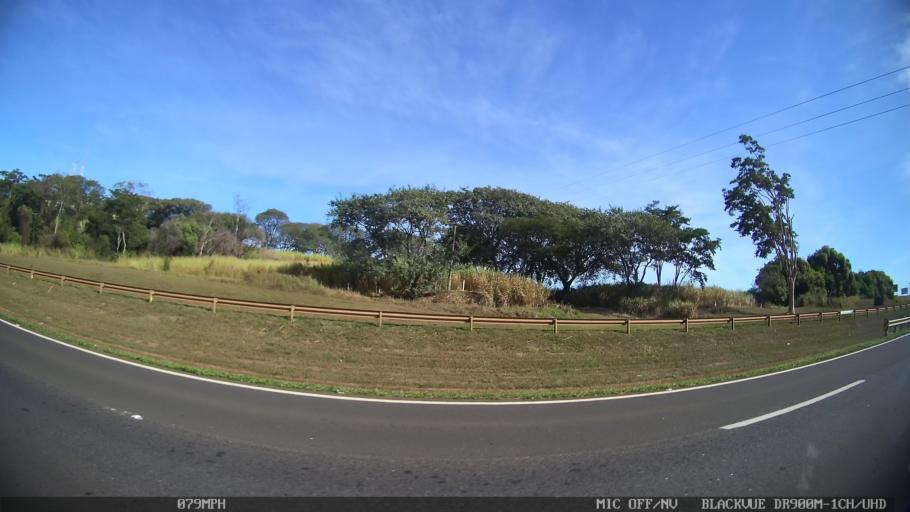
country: BR
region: Sao Paulo
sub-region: Leme
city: Leme
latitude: -22.1546
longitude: -47.4001
